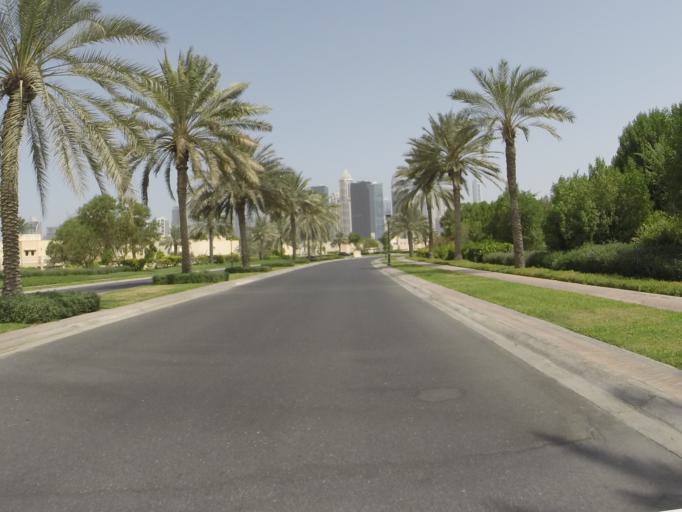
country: AE
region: Dubai
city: Dubai
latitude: 25.0714
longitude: 55.1601
